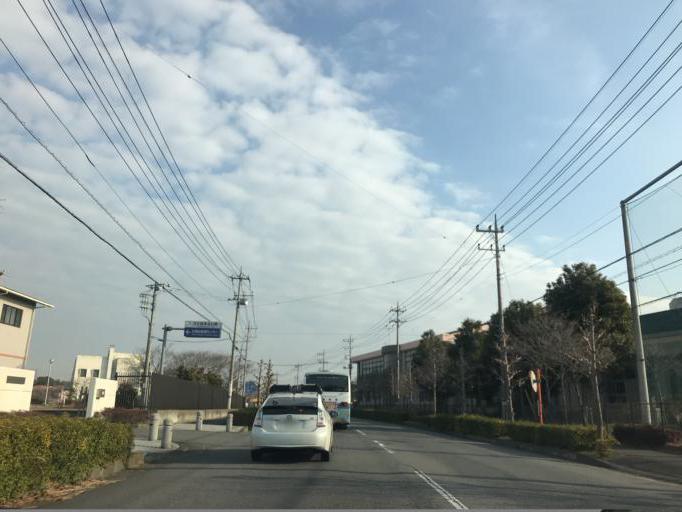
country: JP
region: Ibaraki
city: Mitsukaido
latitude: 35.9801
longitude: 139.9765
